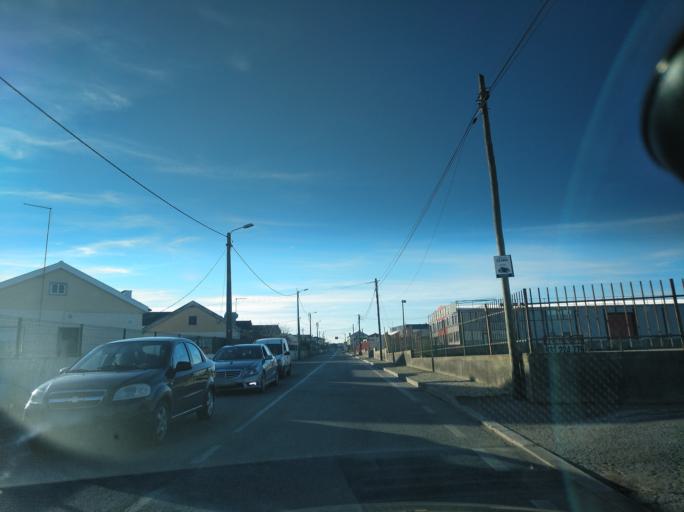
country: PT
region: Lisbon
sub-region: Sintra
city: Sintra
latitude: 38.8354
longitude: -9.3587
